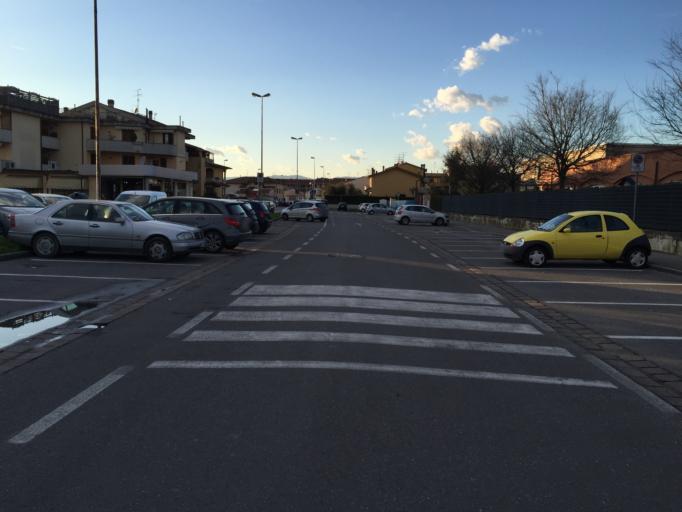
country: IT
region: Tuscany
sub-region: Provincia di Prato
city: Prato
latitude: 43.8844
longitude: 11.0552
